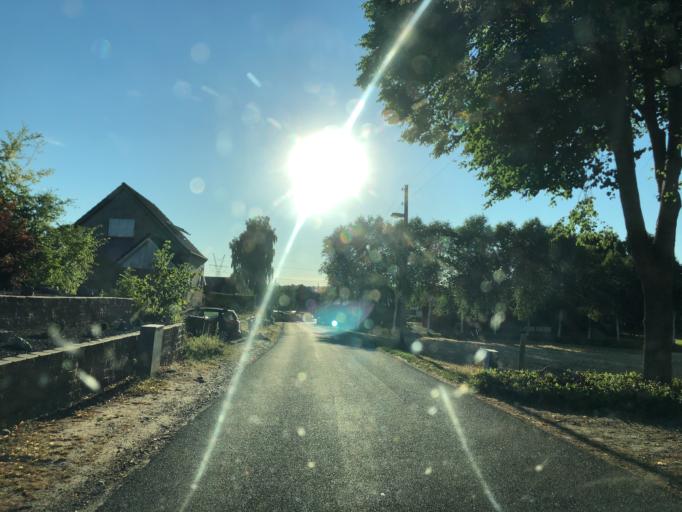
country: DK
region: Central Jutland
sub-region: Horsens Kommune
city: Horsens
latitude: 55.8950
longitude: 9.8469
